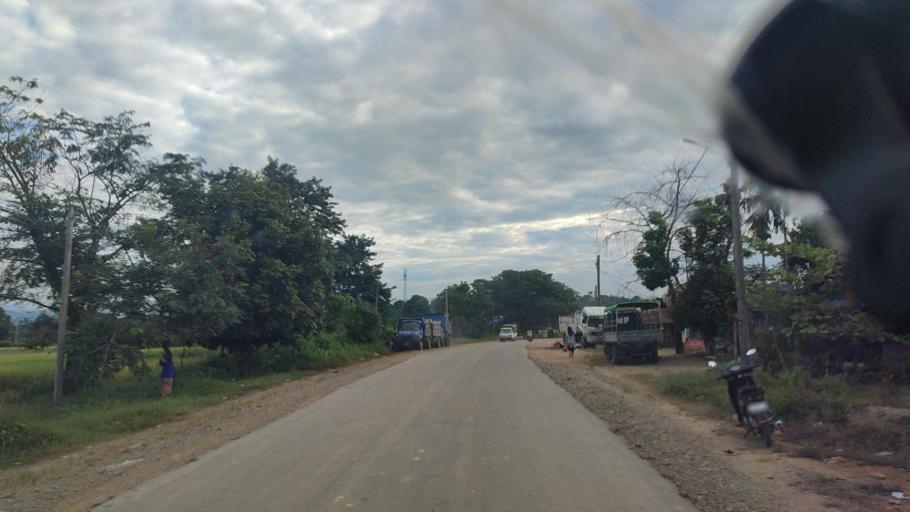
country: MM
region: Magway
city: Minbu
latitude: 19.7634
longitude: 94.0315
